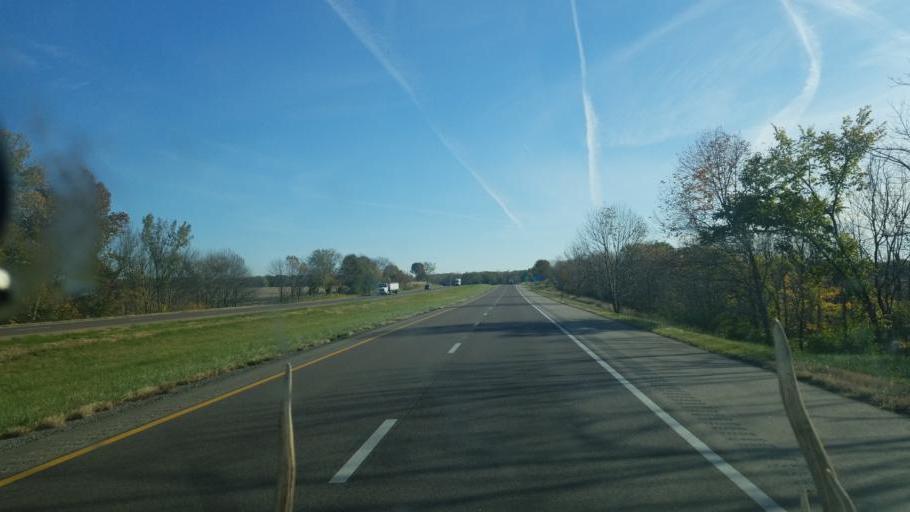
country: US
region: Illinois
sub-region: Madison County
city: Saint Jacob
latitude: 38.7651
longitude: -89.7685
